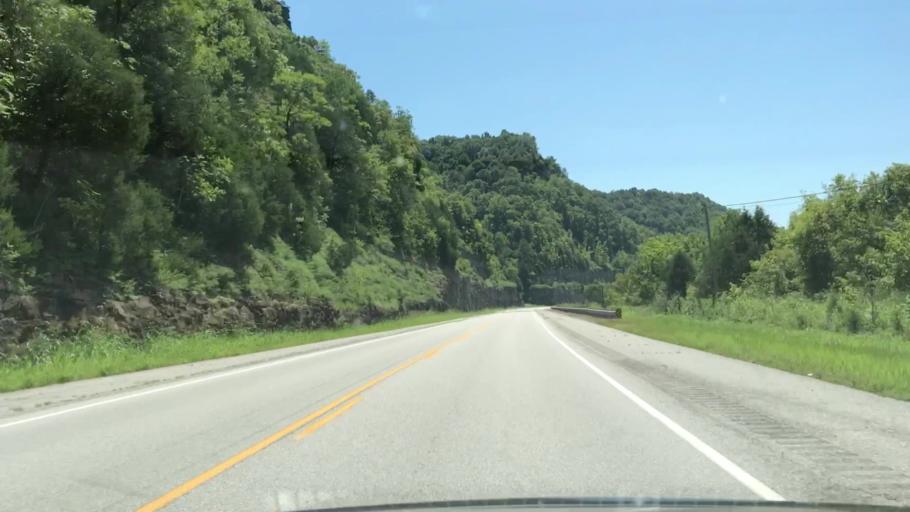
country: US
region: Tennessee
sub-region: Clay County
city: Celina
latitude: 36.4630
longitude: -85.5772
